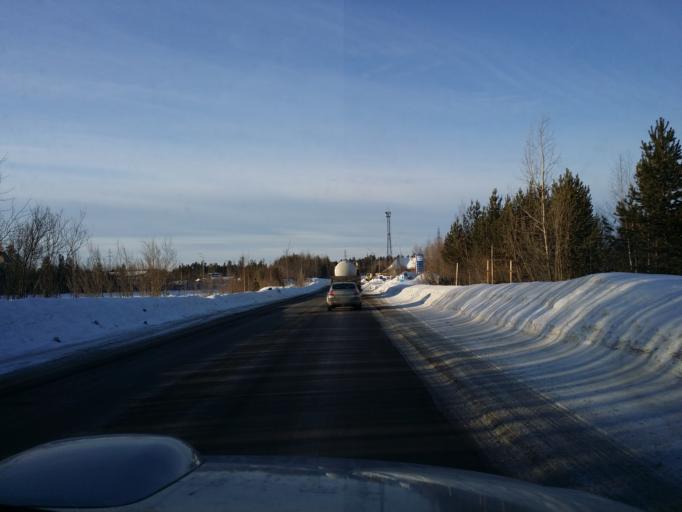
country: RU
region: Khanty-Mansiyskiy Avtonomnyy Okrug
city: Izluchinsk
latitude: 60.9632
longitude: 76.8506
